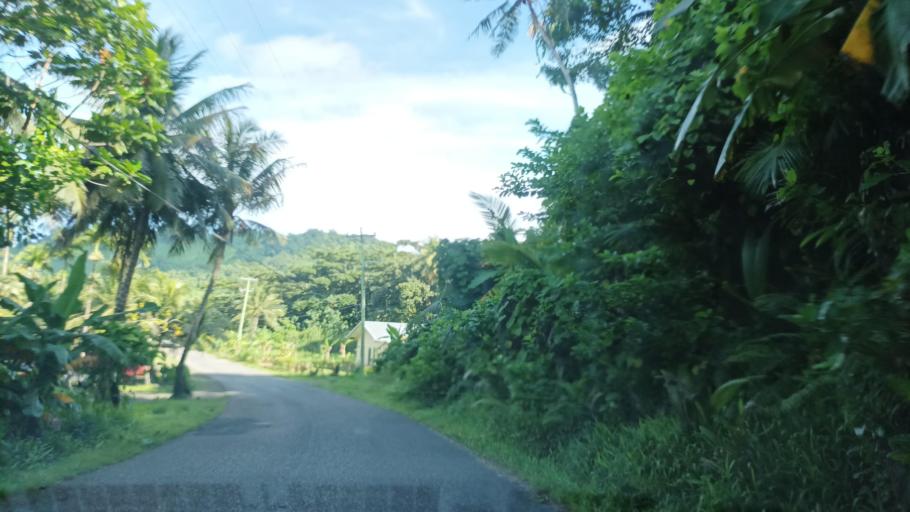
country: FM
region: Kosrae
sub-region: Lelu Municipality
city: Tofol
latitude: 5.3203
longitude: 163.0159
